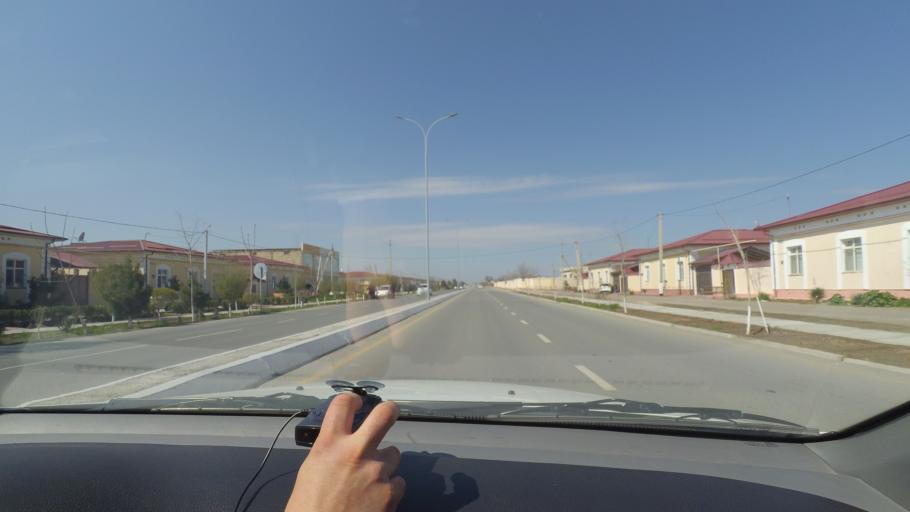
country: UZ
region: Bukhara
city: Galaosiyo
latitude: 39.8037
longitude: 64.5088
